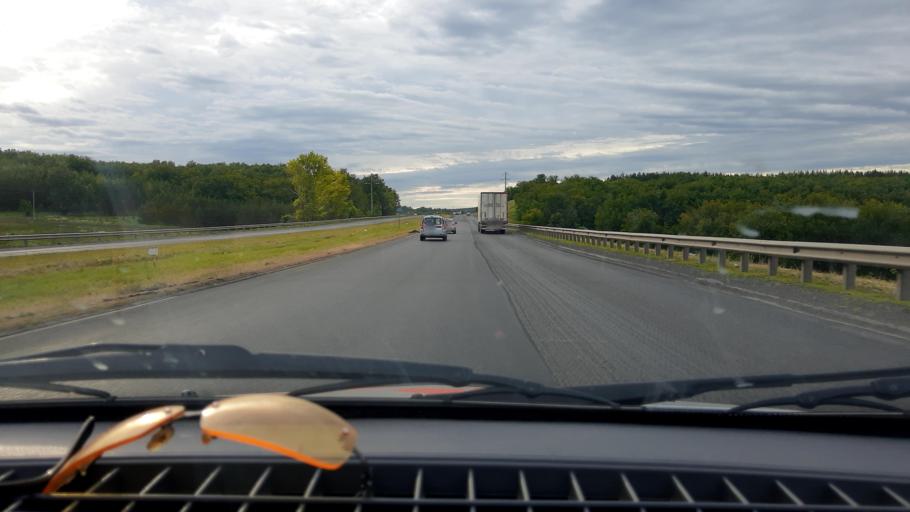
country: RU
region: Bashkortostan
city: Avdon
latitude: 54.6408
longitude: 55.5781
